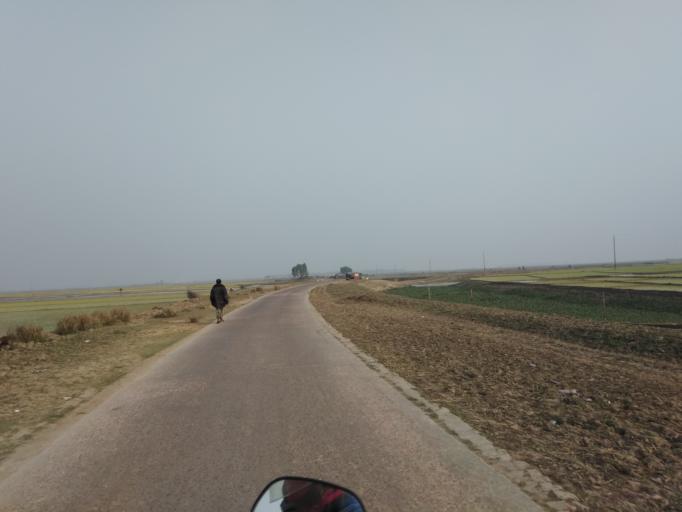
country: BD
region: Rajshahi
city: Ishurdi
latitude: 24.4882
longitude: 89.2071
